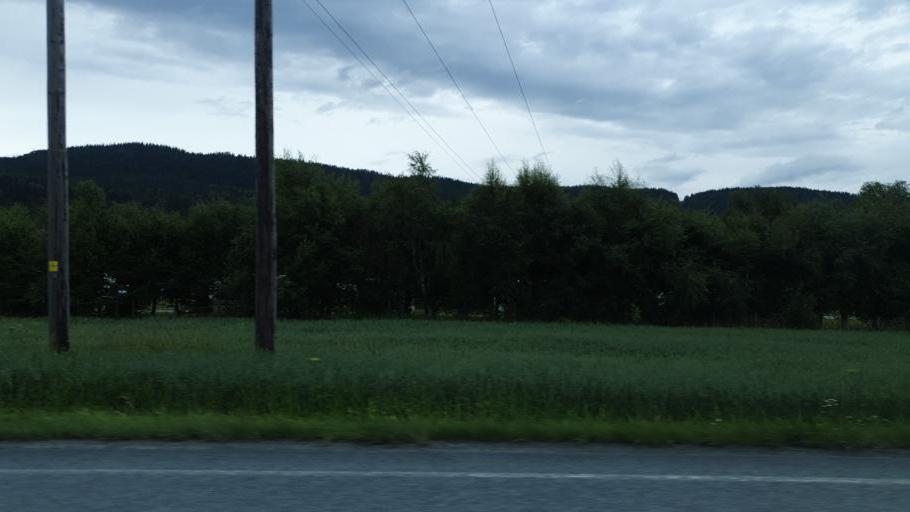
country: NO
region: Sor-Trondelag
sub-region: Melhus
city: Lundamo
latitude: 63.1619
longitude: 10.3018
